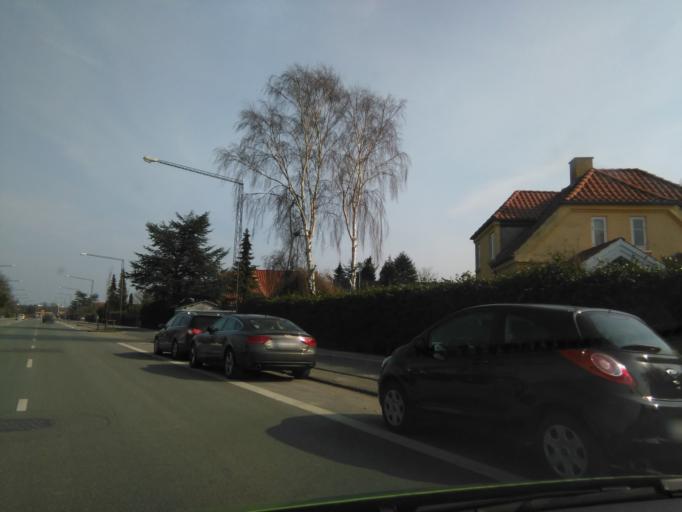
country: DK
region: Central Jutland
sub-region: Arhus Kommune
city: Lystrup
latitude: 56.1985
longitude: 10.2540
